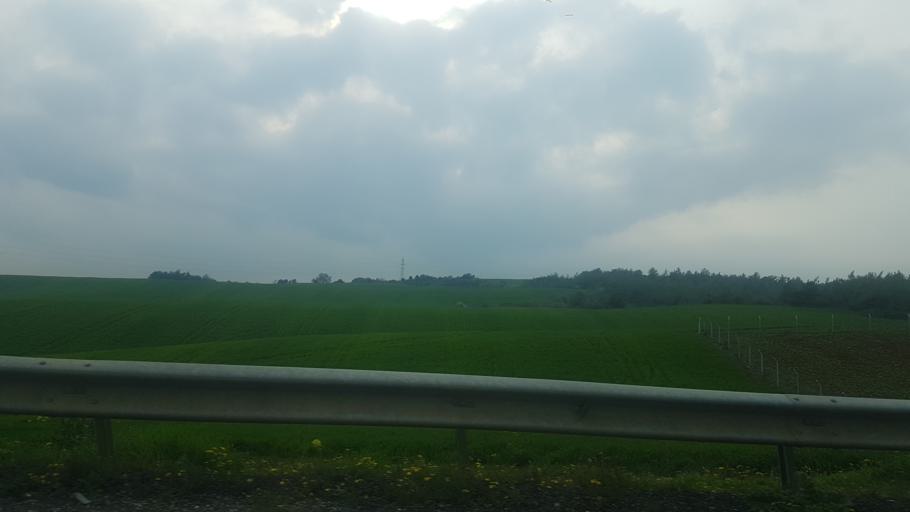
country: TR
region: Mersin
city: Yenice
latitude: 37.0738
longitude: 35.1685
